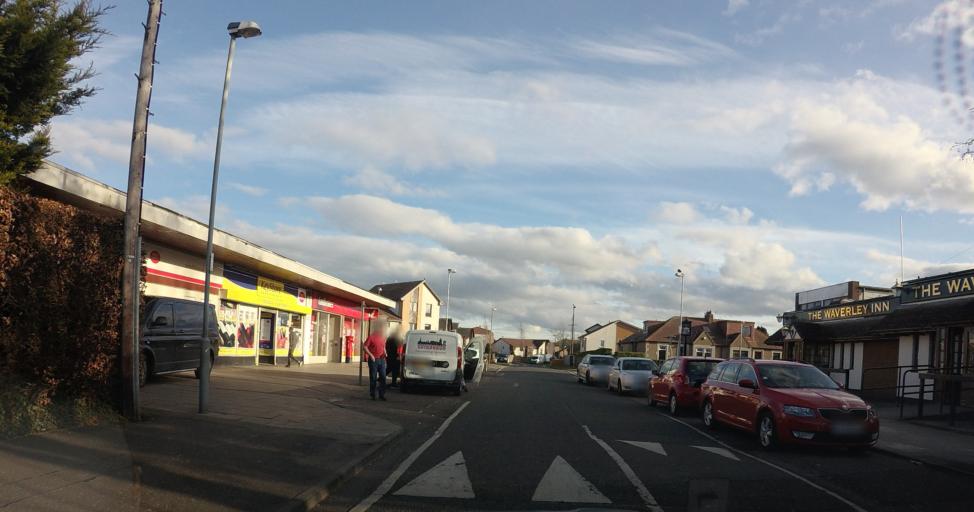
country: GB
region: Scotland
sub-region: Midlothian
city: Loanhead
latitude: 55.9013
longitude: -3.1570
